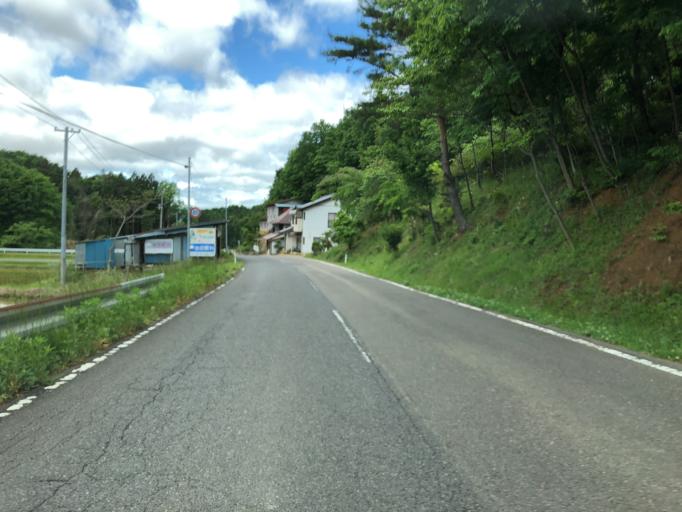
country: JP
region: Fukushima
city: Miharu
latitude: 37.4700
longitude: 140.4640
